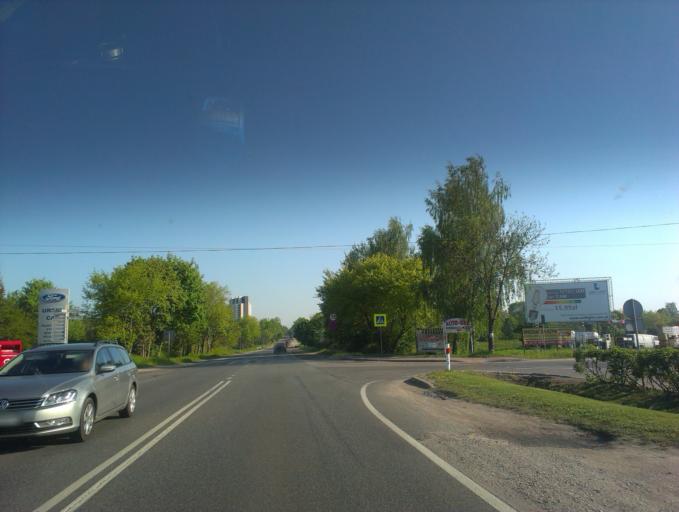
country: PL
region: Masovian Voivodeship
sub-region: Powiat piaseczynski
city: Piaseczno
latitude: 52.0710
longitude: 21.0358
